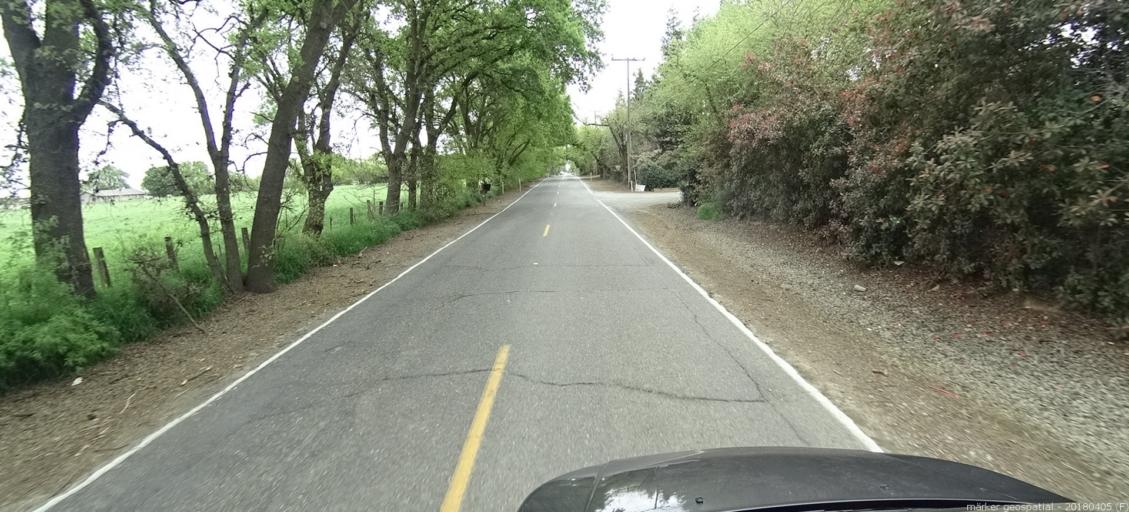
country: US
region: California
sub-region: Sacramento County
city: Galt
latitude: 38.2473
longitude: -121.3401
